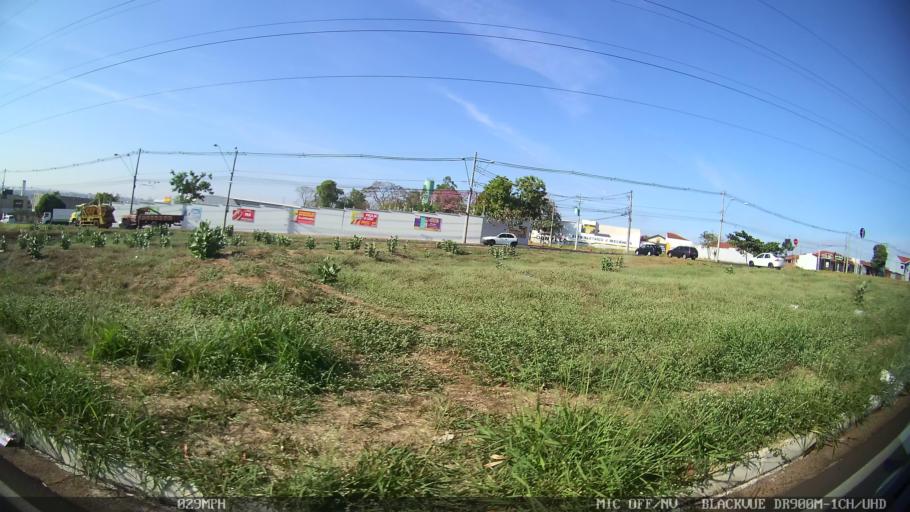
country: BR
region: Sao Paulo
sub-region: Sao Jose Do Rio Preto
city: Sao Jose do Rio Preto
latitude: -20.7687
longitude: -49.3880
